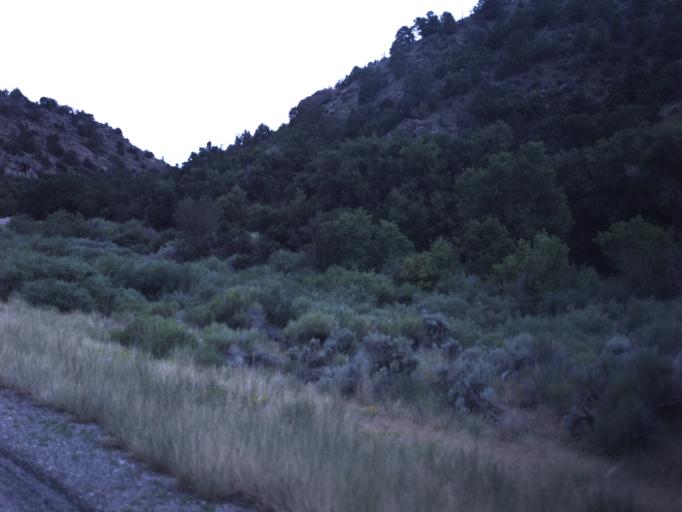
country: US
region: Utah
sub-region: Sevier County
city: Richfield
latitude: 38.7368
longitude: -111.9166
